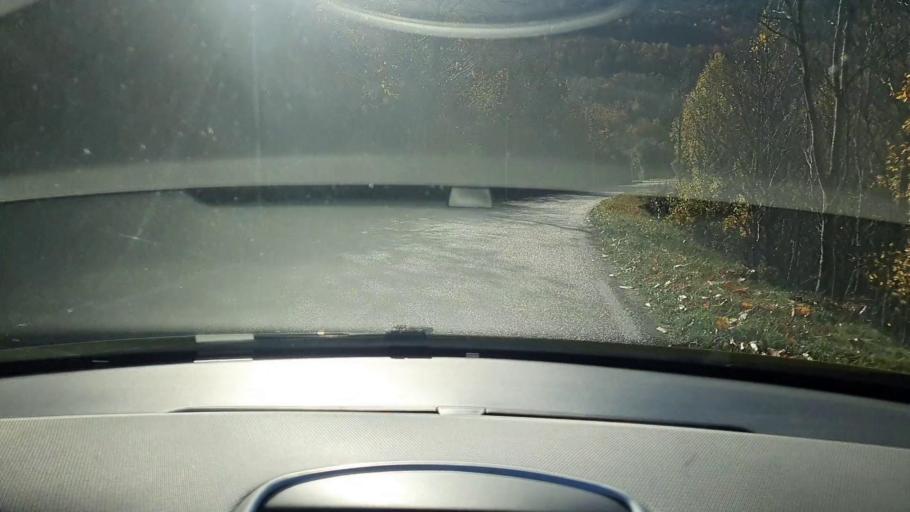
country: FR
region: Languedoc-Roussillon
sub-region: Departement du Gard
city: Valleraugue
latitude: 44.1618
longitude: 3.6556
